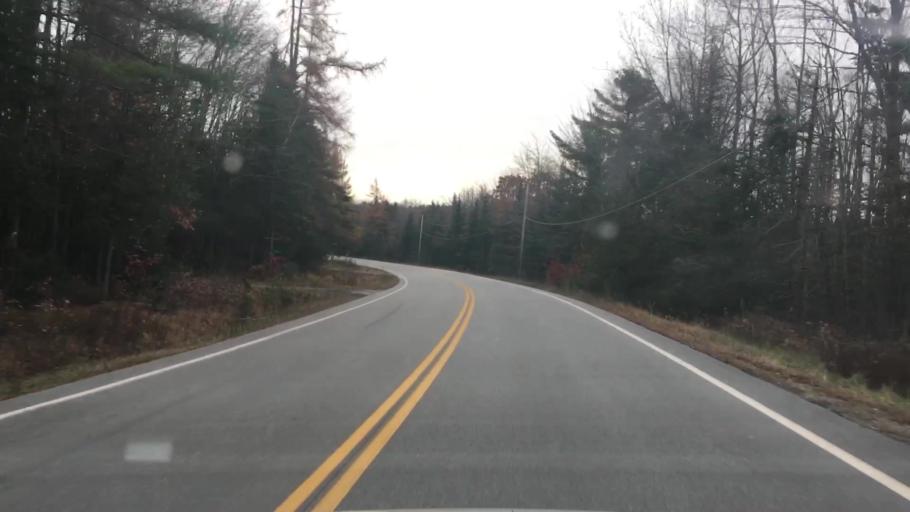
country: US
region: Maine
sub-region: Hancock County
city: Penobscot
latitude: 44.5046
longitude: -68.6553
